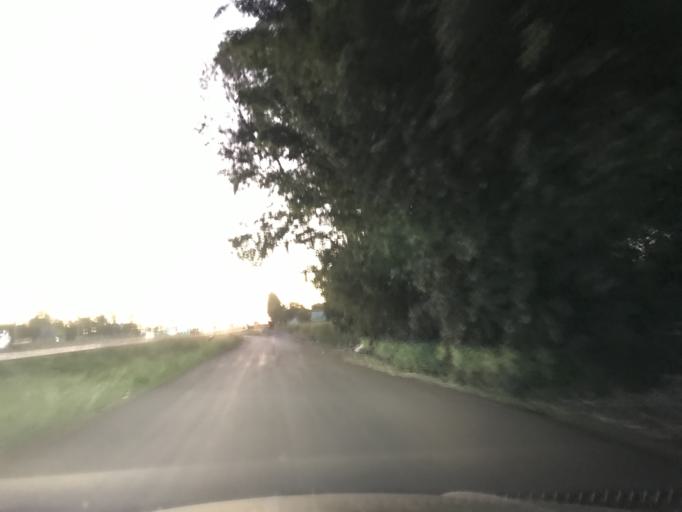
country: BR
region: Parana
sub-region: Toledo
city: Toledo
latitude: -24.8217
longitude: -53.6525
